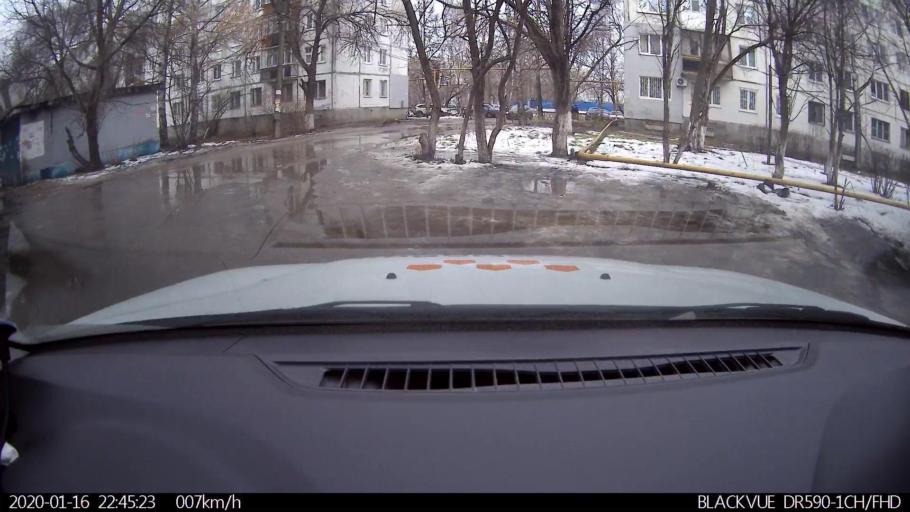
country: RU
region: Nizjnij Novgorod
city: Nizhniy Novgorod
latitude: 56.2842
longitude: 43.9233
